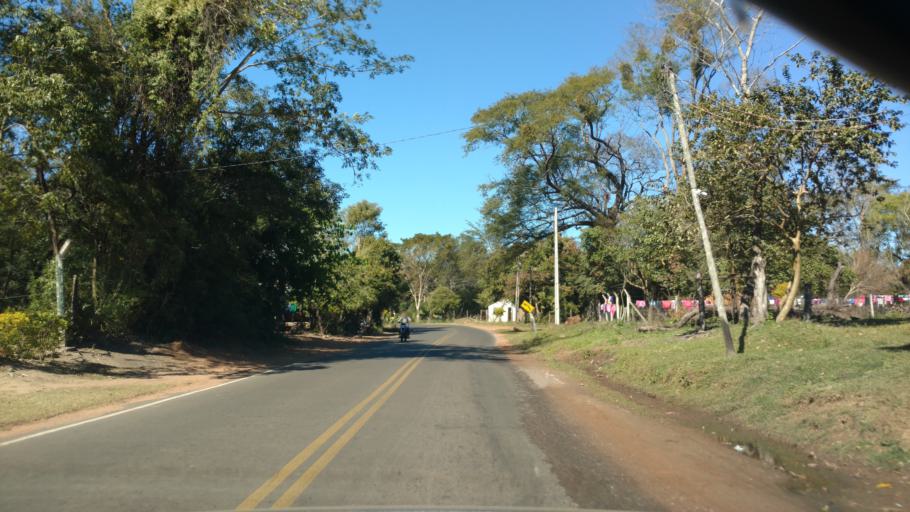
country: PY
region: Central
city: Ypacarai
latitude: -25.4217
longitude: -57.2936
